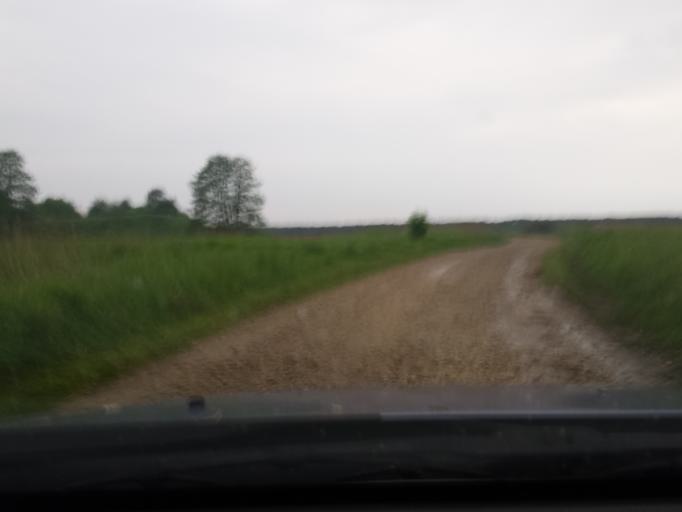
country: LV
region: Riga
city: Bolderaja
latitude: 57.0551
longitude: 24.0960
